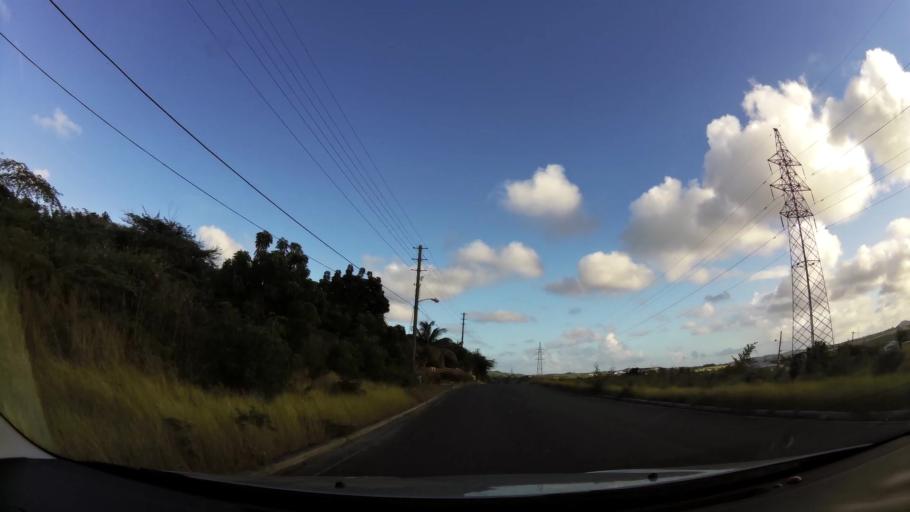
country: AG
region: Saint George
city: Piggotts
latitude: 17.1163
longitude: -61.7947
